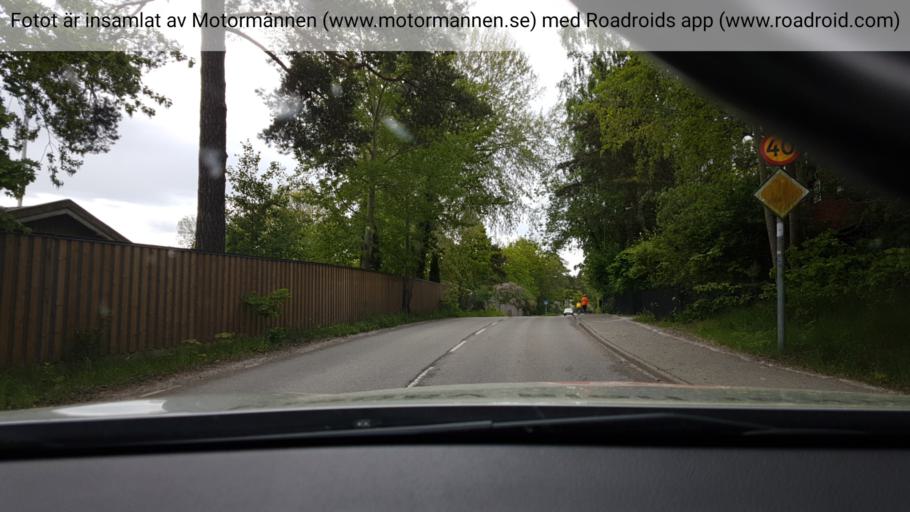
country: SE
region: Stockholm
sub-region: Nacka Kommun
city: Saltsjobaden
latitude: 59.2817
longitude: 18.2863
